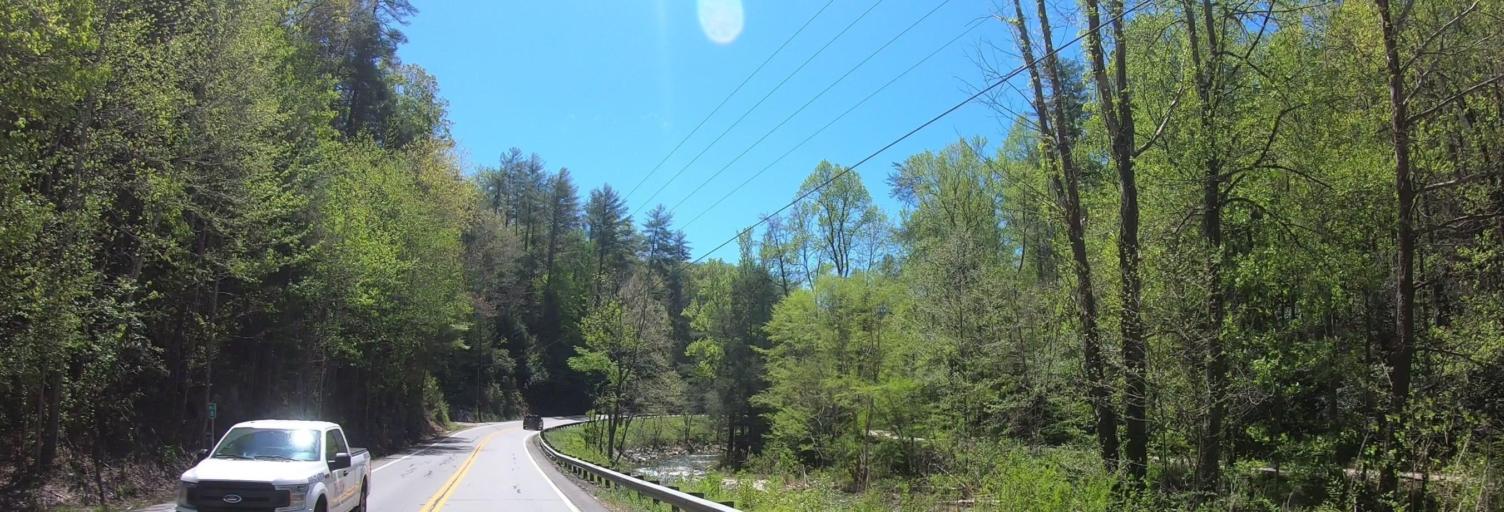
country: US
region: Georgia
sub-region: White County
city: Cleveland
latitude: 34.7204
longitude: -83.7474
